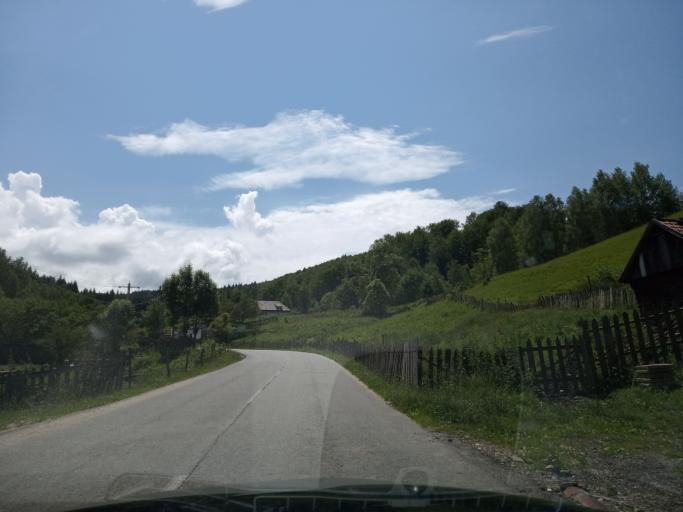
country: RO
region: Hunedoara
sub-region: Oras Petrila
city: Petrila
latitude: 45.4027
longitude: 23.4143
